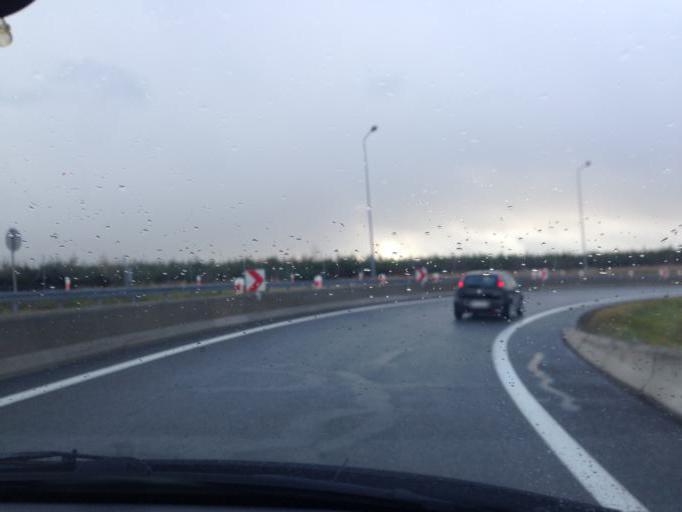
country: PL
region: Opole Voivodeship
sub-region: Powiat strzelecki
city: Ujazd
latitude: 50.4454
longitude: 18.3476
